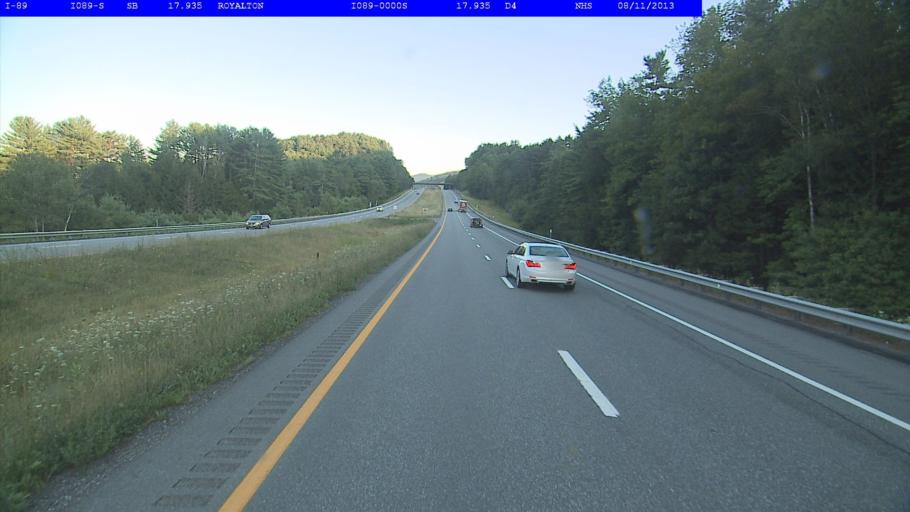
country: US
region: Vermont
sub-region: Orange County
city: Randolph
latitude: 43.8132
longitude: -72.5220
